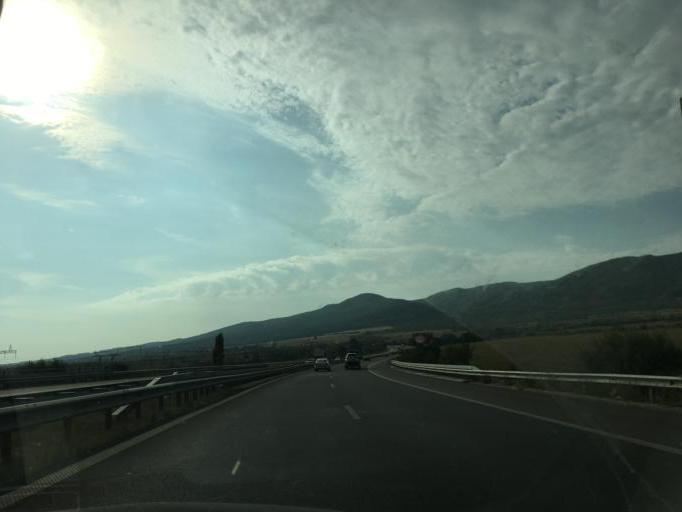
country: BG
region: Sofiya
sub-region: Obshtina Elin Pelin
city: Elin Pelin
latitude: 42.6224
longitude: 23.5204
